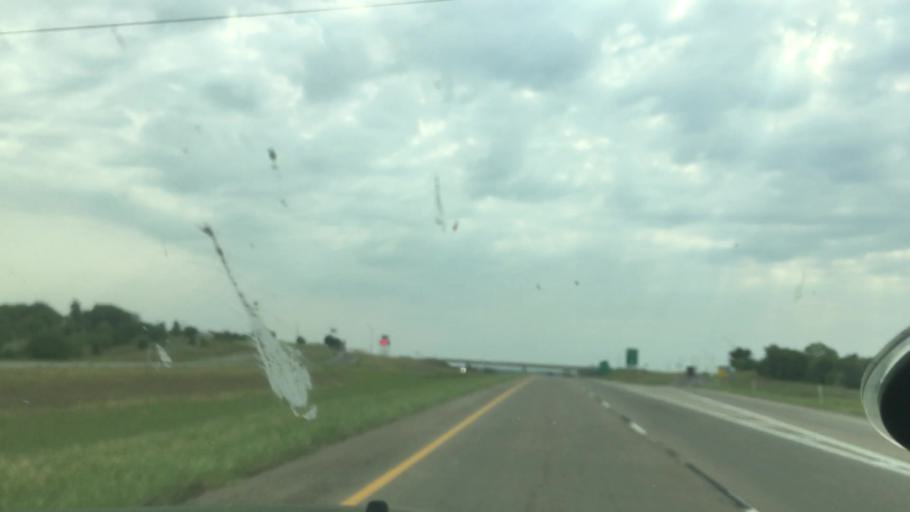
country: US
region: Texas
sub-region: Grayson County
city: Denison
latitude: 33.7930
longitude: -96.5608
